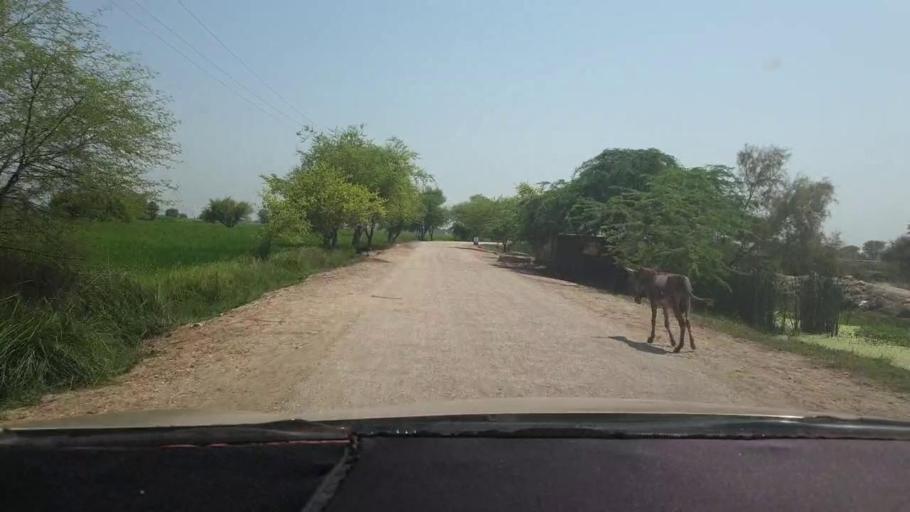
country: PK
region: Sindh
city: Miro Khan
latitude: 27.6812
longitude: 68.0957
